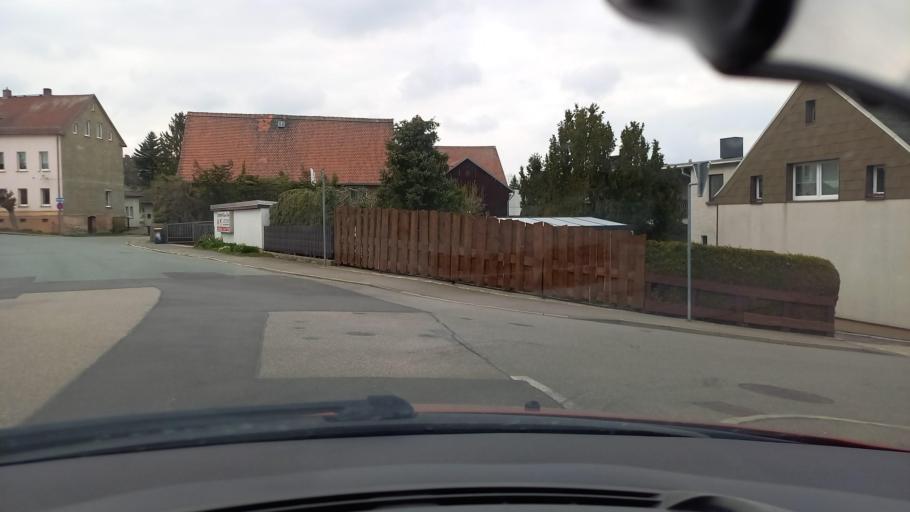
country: DE
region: Saxony
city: Wilkau-Hasslau
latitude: 50.6730
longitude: 12.4907
